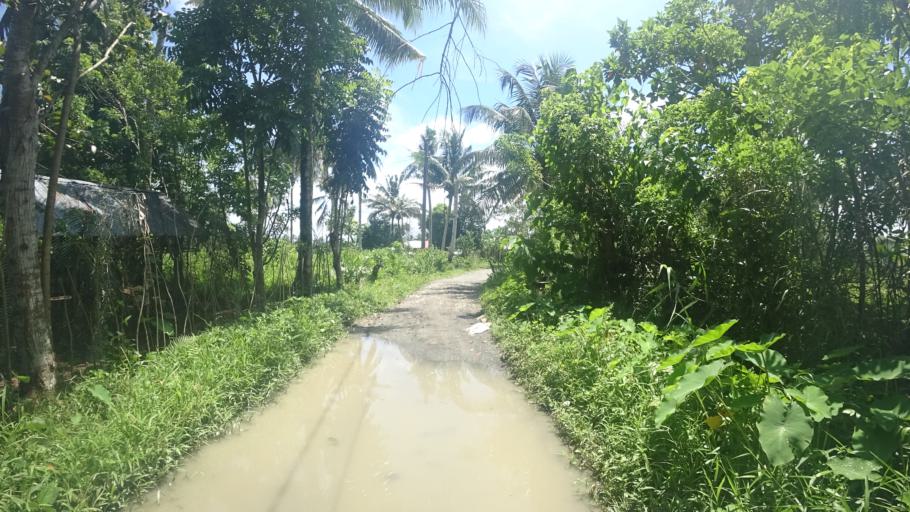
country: PH
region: Eastern Visayas
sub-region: Province of Leyte
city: Alangalang
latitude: 11.2330
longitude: 124.8447
